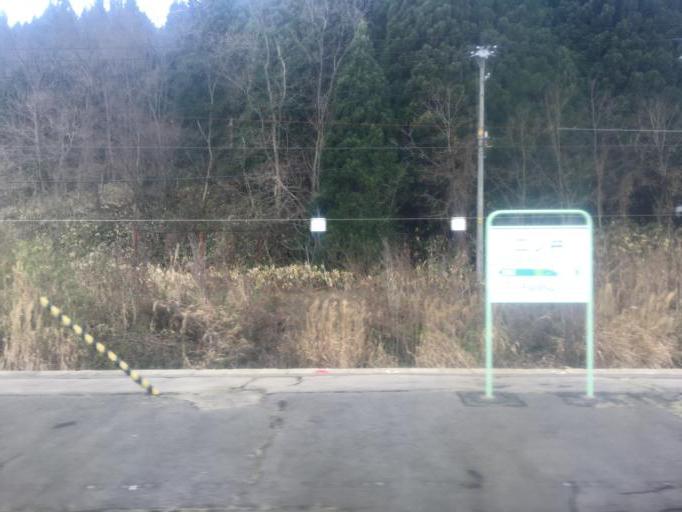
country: JP
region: Akita
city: Takanosu
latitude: 40.2127
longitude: 140.2358
